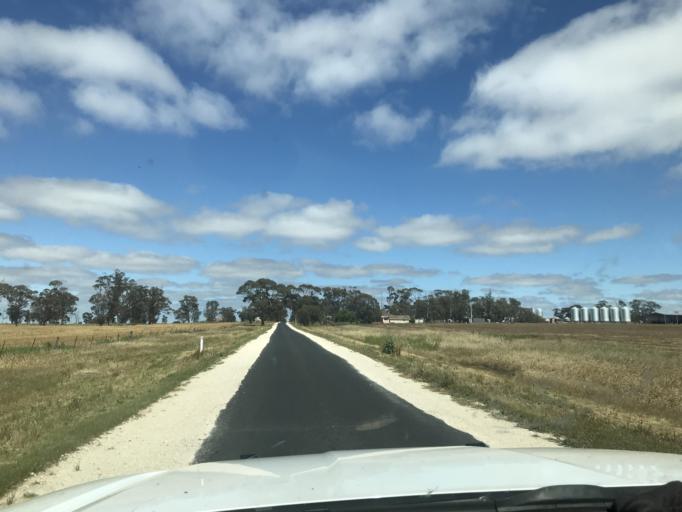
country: AU
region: South Australia
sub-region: Tatiara
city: Bordertown
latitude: -36.3061
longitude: 141.0797
